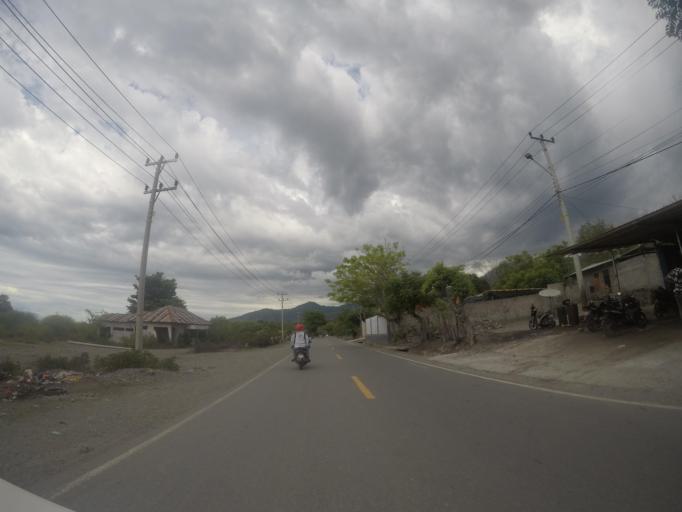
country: TL
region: Liquica
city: Liquica
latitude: -8.5964
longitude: 125.3187
